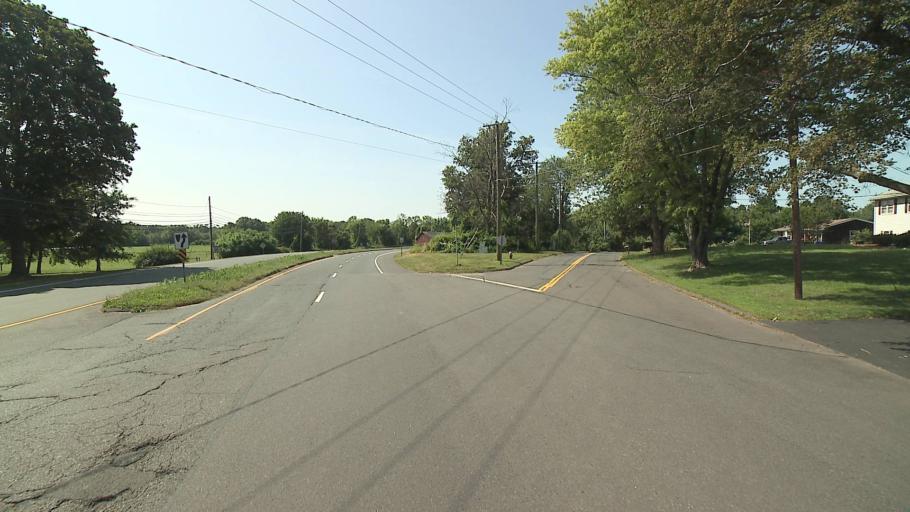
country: US
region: Connecticut
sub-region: Hartford County
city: Enfield
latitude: 41.9638
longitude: -72.5934
